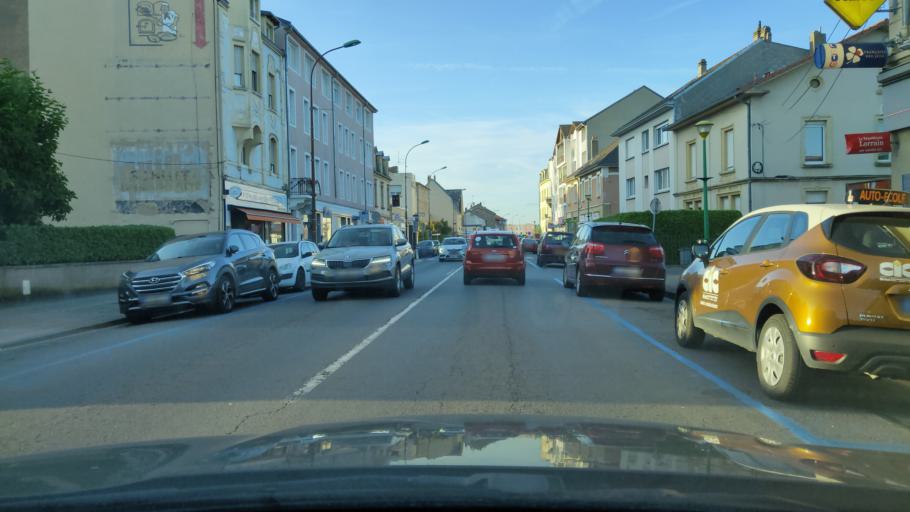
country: FR
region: Lorraine
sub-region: Departement de la Moselle
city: Maizieres-les-Metz
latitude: 49.2123
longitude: 6.1597
